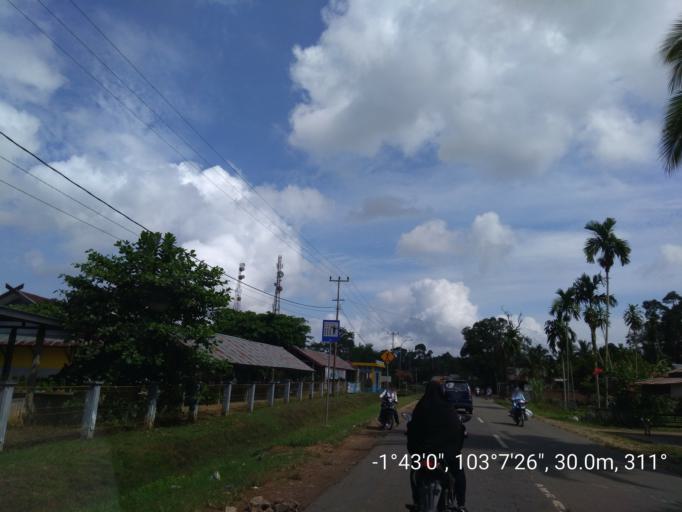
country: ID
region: Jambi
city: Muara Tembesi
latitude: -1.7168
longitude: 103.1239
